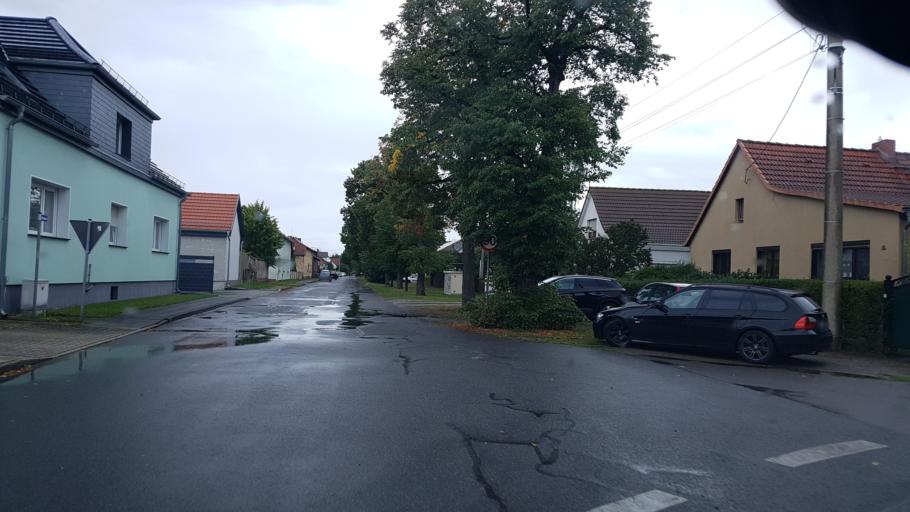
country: DE
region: Brandenburg
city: Grossraschen
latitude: 51.5876
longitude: 14.0368
